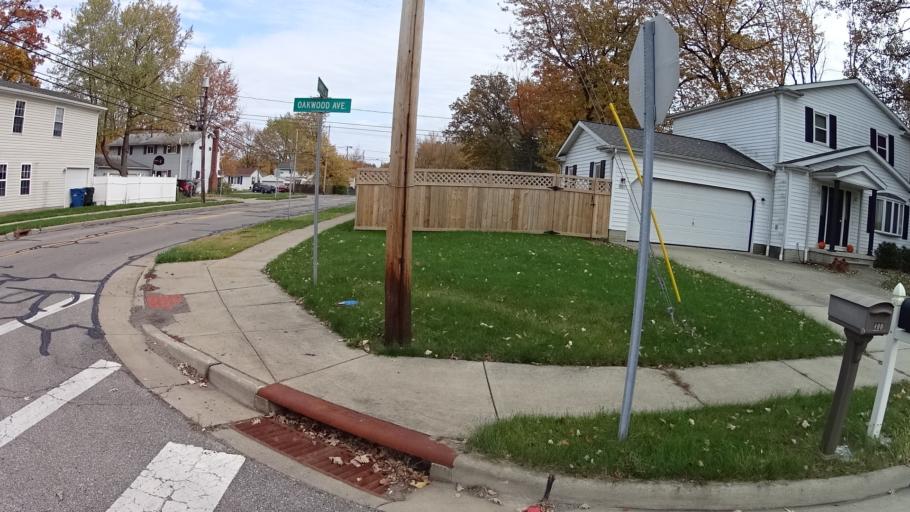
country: US
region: Ohio
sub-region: Lorain County
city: Sheffield Lake
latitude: 41.4848
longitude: -82.0985
